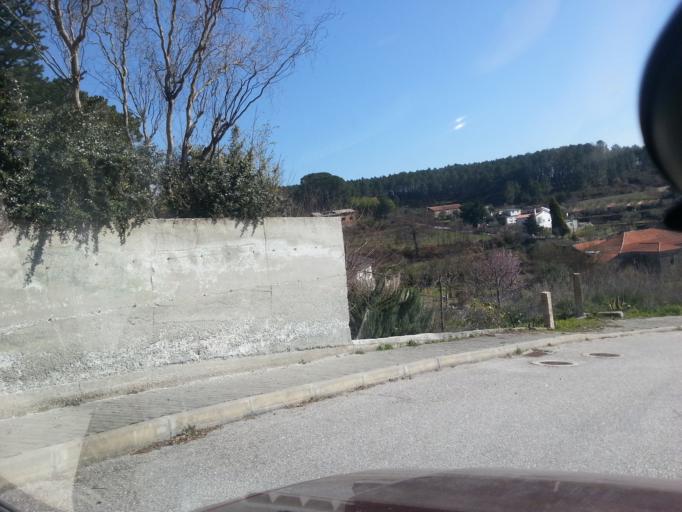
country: PT
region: Guarda
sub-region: Fornos de Algodres
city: Fornos de Algodres
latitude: 40.6261
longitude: -7.5301
